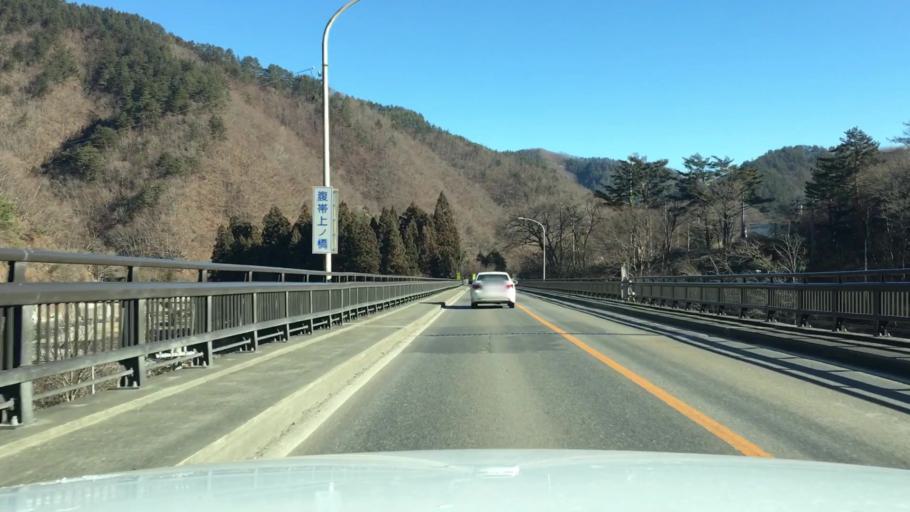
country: JP
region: Iwate
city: Miyako
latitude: 39.6005
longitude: 141.7617
